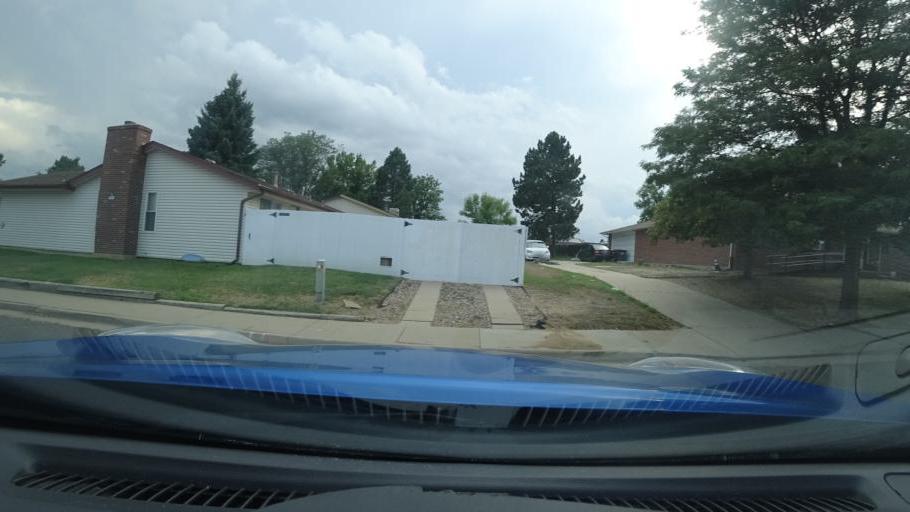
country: US
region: Colorado
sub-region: Adams County
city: Aurora
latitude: 39.6944
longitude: -104.8151
